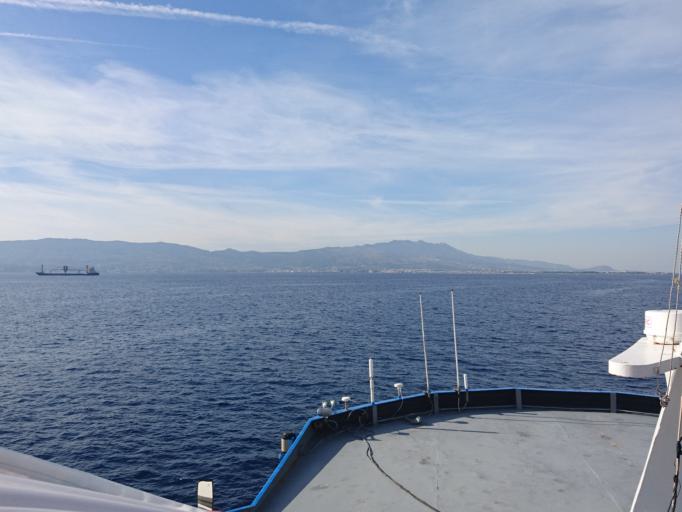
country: GR
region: South Aegean
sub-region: Nomos Dodekanisou
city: Kos
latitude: 36.9358
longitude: 27.3306
